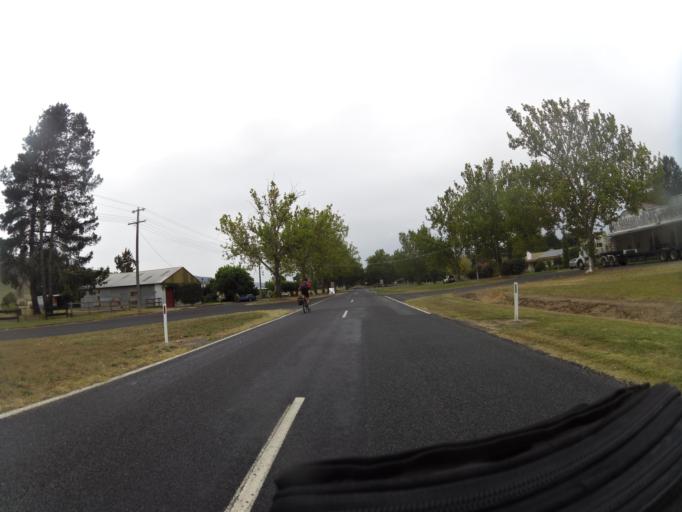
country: AU
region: New South Wales
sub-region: Greater Hume Shire
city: Holbrook
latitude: -36.1917
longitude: 147.7701
